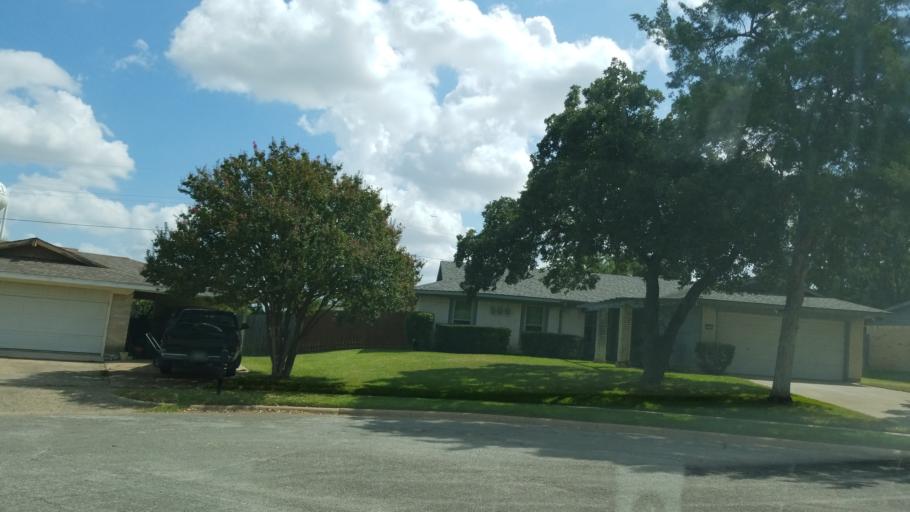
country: US
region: Texas
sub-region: Tarrant County
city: Euless
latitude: 32.8559
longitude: -97.0853
